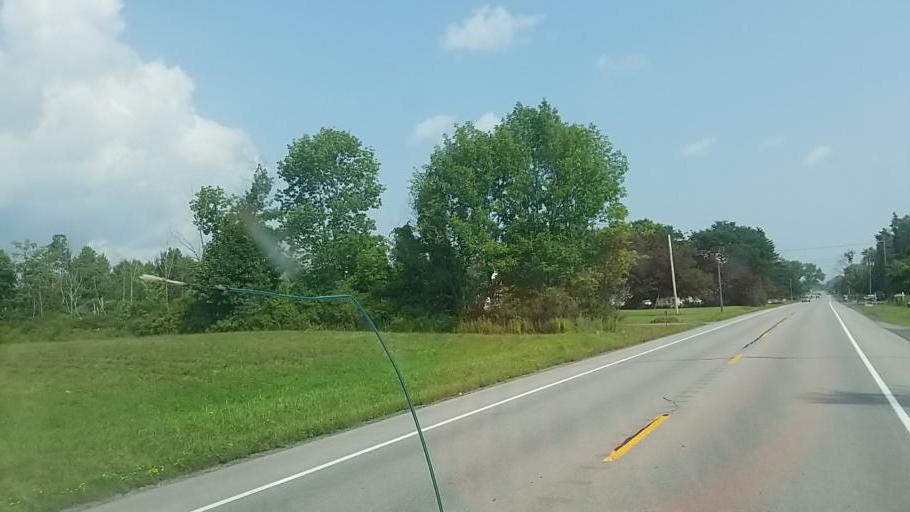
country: US
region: New York
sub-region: Fulton County
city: Johnstown
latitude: 42.9924
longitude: -74.3351
